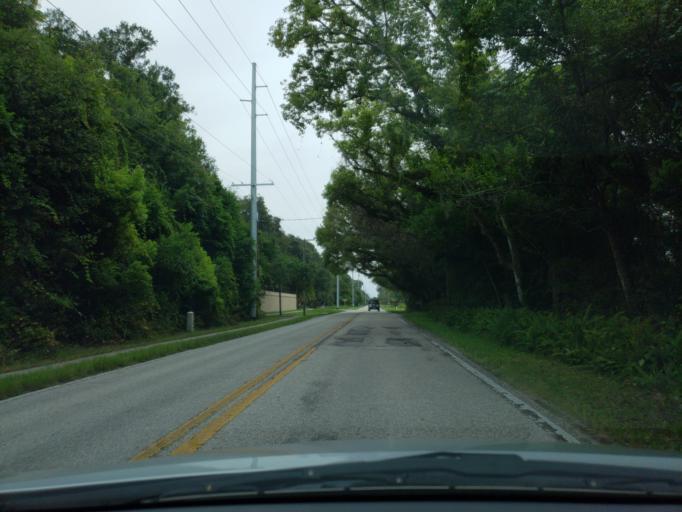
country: US
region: Florida
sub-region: Hillsborough County
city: Lutz
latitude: 28.1424
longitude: -82.4583
